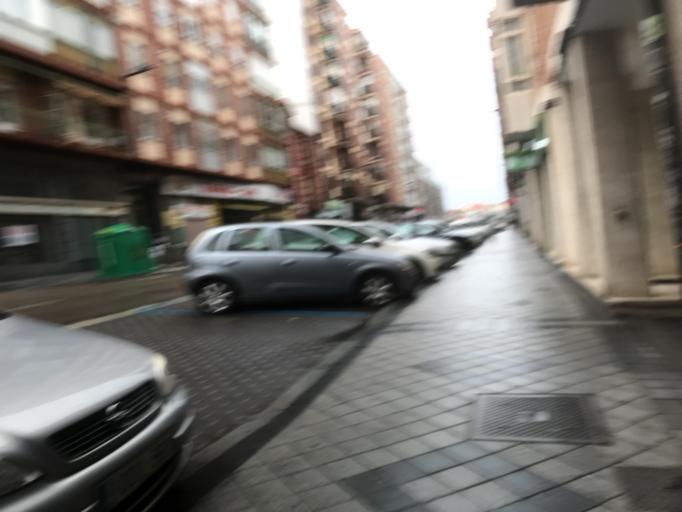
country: ES
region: Castille and Leon
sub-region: Provincia de Valladolid
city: Valladolid
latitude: 41.6456
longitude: -4.7222
